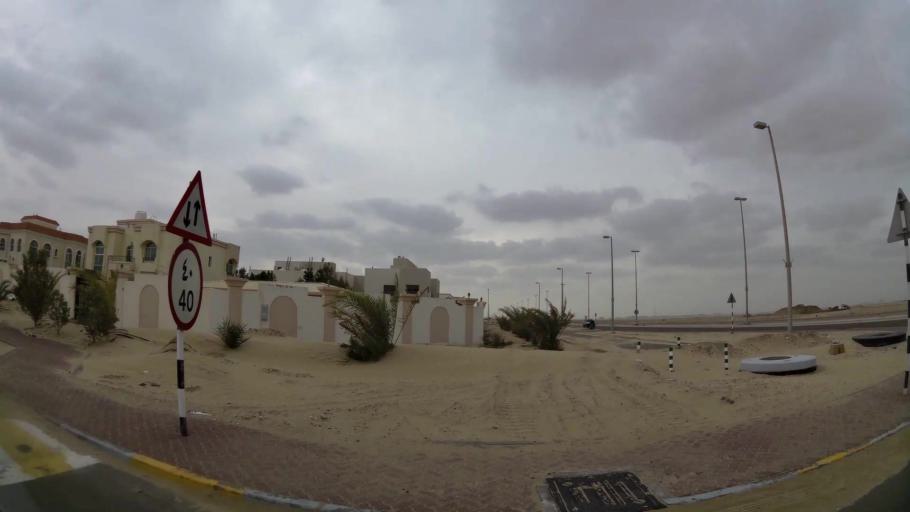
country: AE
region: Abu Dhabi
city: Abu Dhabi
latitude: 24.3727
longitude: 54.6268
